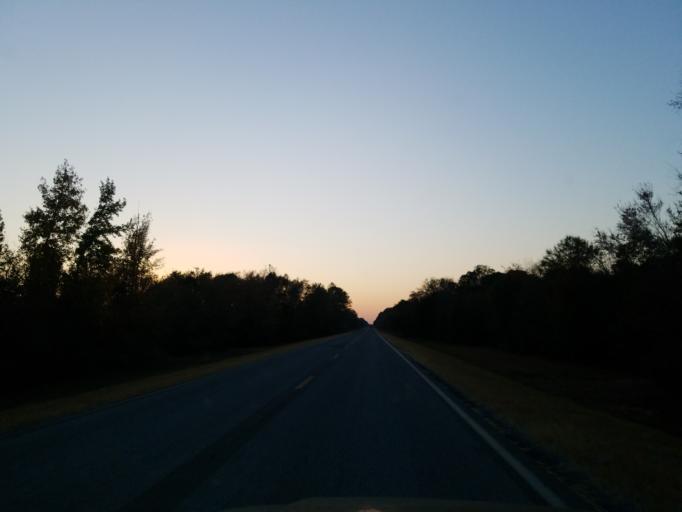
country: US
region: Georgia
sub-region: Ben Hill County
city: Fitzgerald
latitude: 31.7210
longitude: -83.4475
